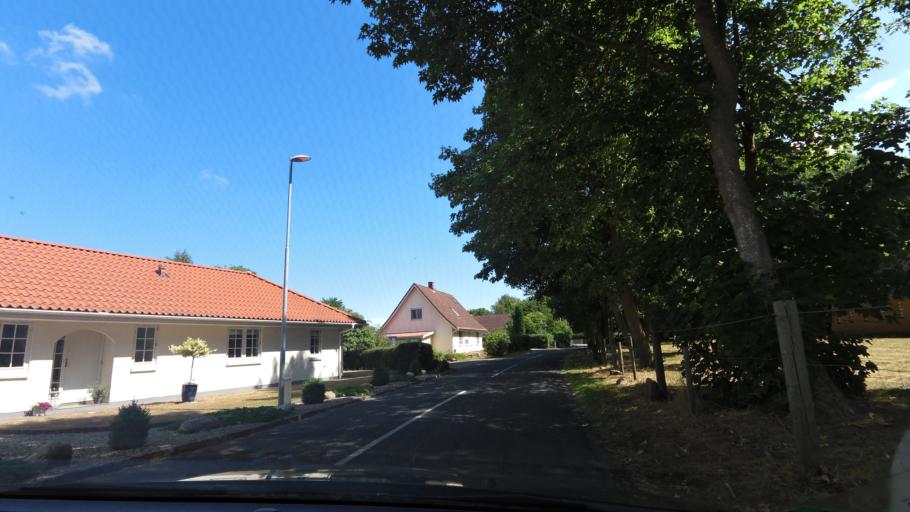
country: DK
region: South Denmark
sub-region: Nordfyns Kommune
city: Otterup
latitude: 55.5506
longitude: 10.4612
